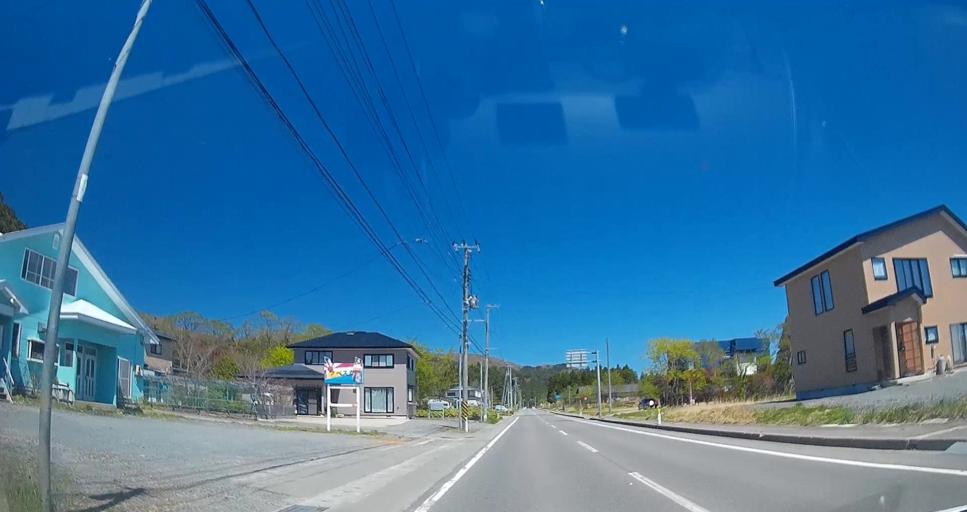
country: JP
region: Aomori
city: Mutsu
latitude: 41.0828
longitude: 141.3858
